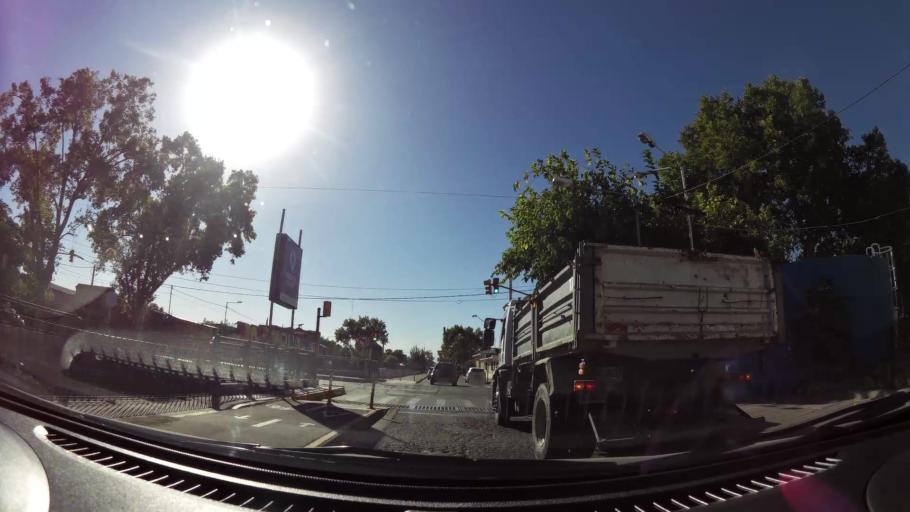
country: AR
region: Mendoza
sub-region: Departamento de Godoy Cruz
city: Godoy Cruz
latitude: -32.9226
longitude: -68.8445
